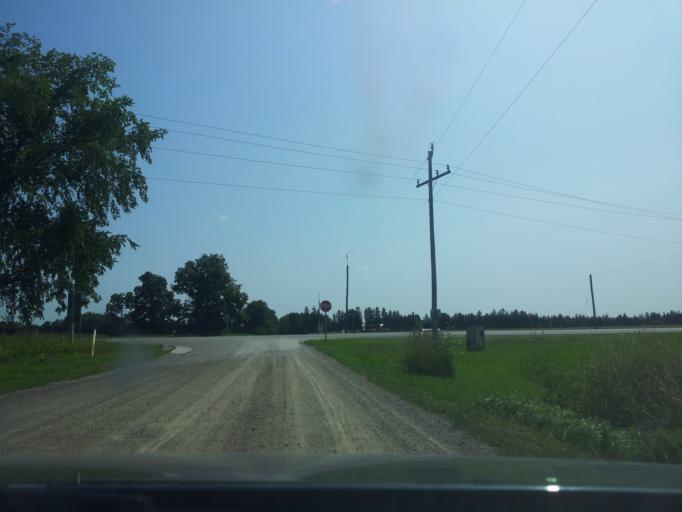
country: CA
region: Ontario
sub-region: Oxford County
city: Woodstock
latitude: 42.9585
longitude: -80.5902
